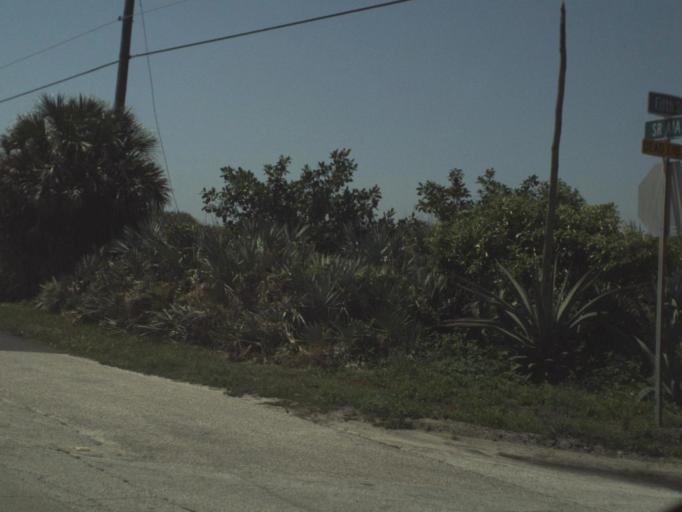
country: US
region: Florida
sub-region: Brevard County
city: Malabar
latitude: 28.0242
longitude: -80.5371
